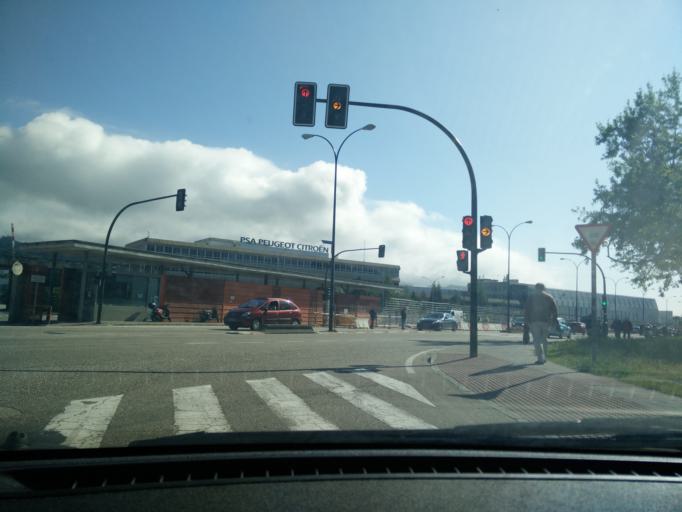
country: ES
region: Galicia
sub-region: Provincia de Pontevedra
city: Vigo
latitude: 42.2106
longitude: -8.7406
